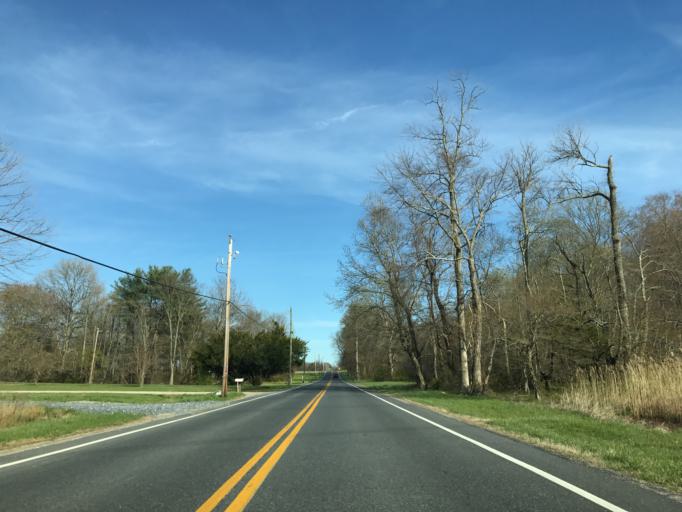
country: US
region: Maryland
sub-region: Caroline County
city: Greensboro
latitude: 39.0348
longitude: -75.7746
